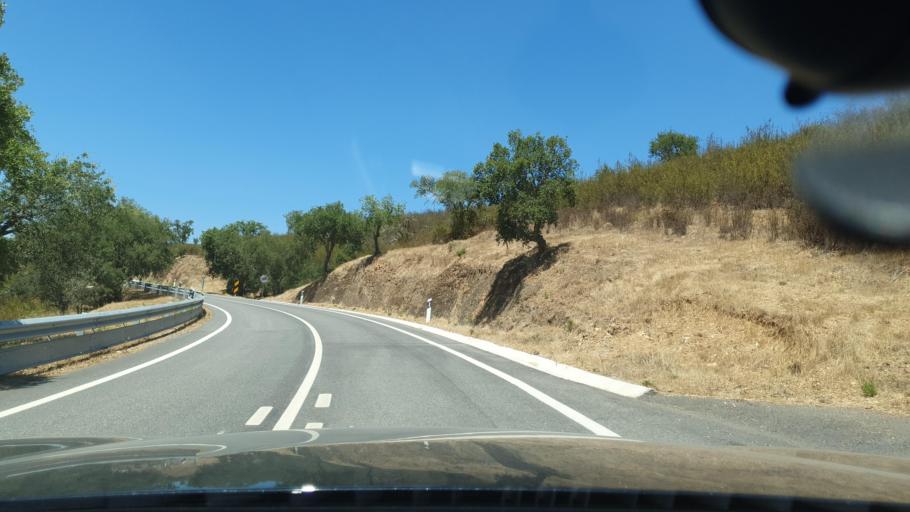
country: PT
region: Beja
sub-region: Odemira
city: Odemira
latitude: 37.5256
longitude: -8.4741
